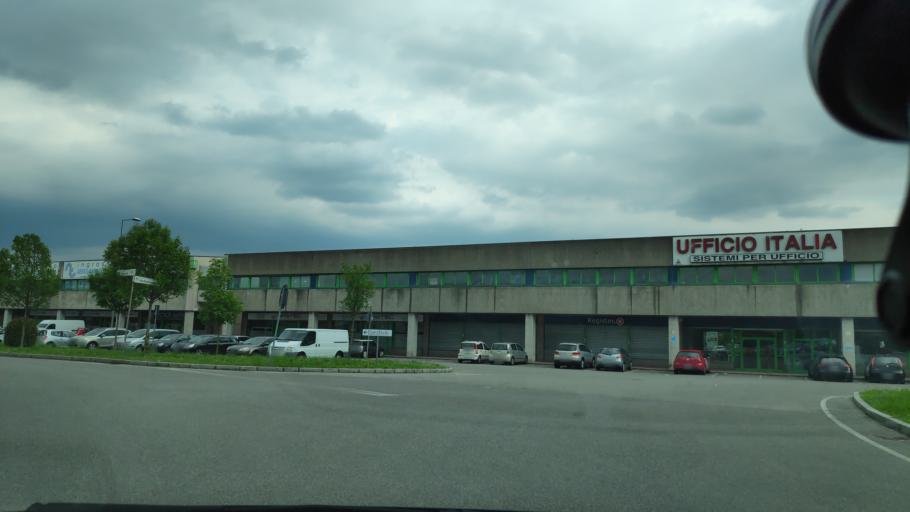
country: IT
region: Lombardy
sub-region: Provincia di Bergamo
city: Azzano San Paolo
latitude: 45.6713
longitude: 9.6753
